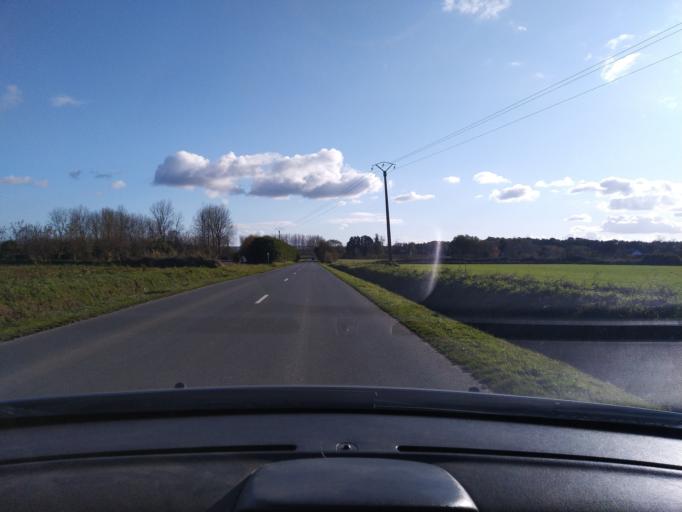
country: FR
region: Brittany
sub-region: Departement des Cotes-d'Armor
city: Plestin-les-Greves
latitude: 48.6315
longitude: -3.6169
